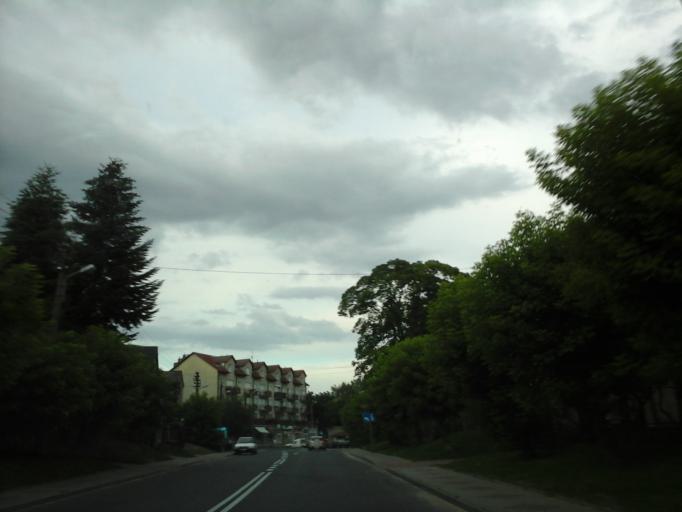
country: PL
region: West Pomeranian Voivodeship
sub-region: Powiat goleniowski
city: Nowogard
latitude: 53.6752
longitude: 15.1126
